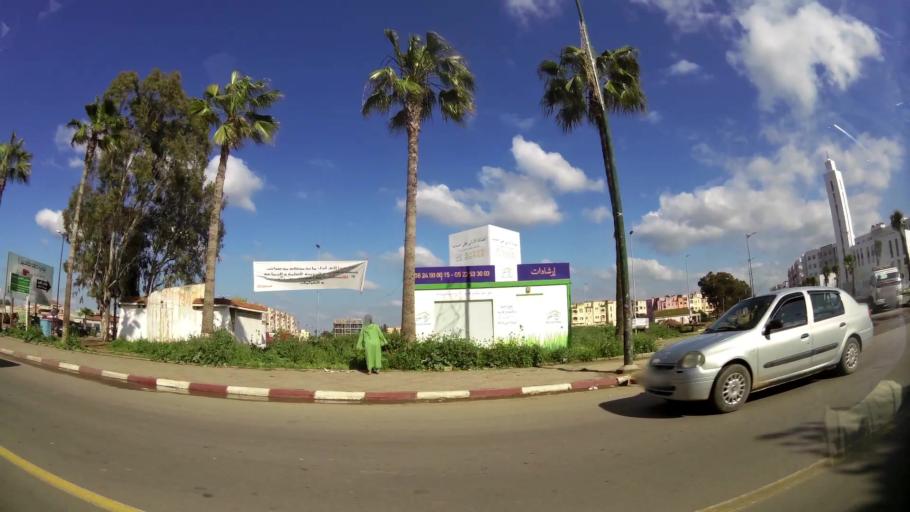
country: MA
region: Chaouia-Ouardigha
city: Nouaseur
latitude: 33.3724
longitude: -7.5419
